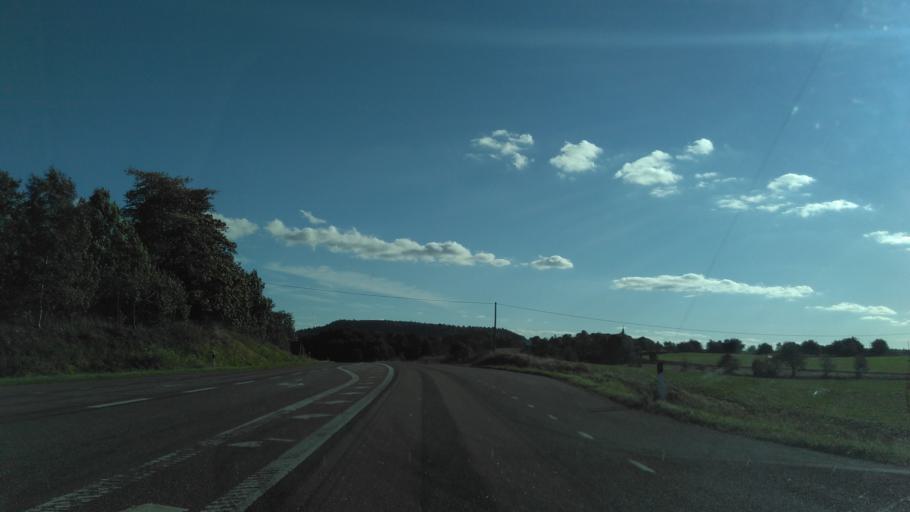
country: SE
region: Vaestra Goetaland
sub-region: Skovde Kommun
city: Skultorp
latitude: 58.3262
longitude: 13.8142
